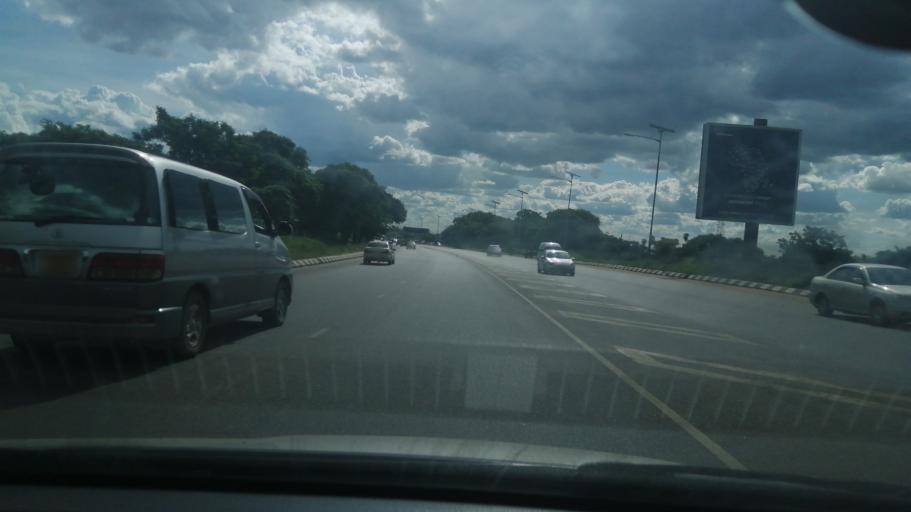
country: ZW
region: Harare
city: Harare
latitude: -17.8500
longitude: 31.0588
